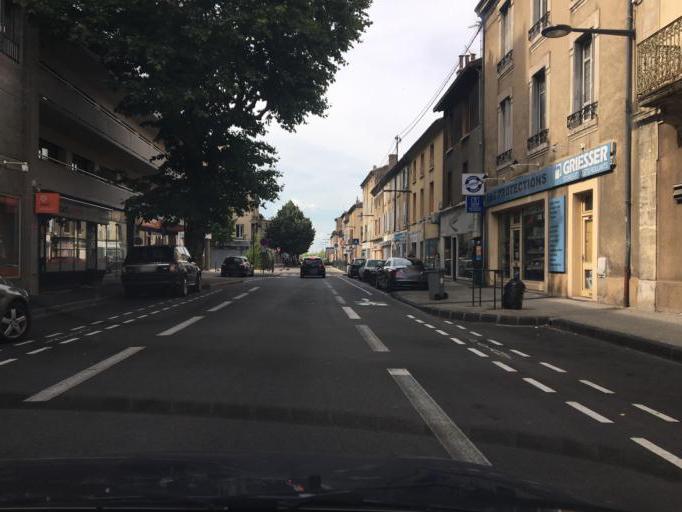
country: FR
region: Rhone-Alpes
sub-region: Departement de la Drome
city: Valence
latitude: 44.9354
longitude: 4.8971
